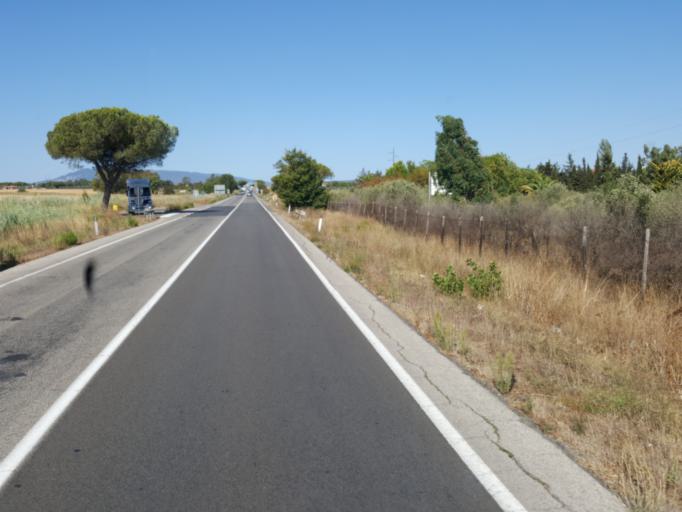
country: IT
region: Tuscany
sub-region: Provincia di Grosseto
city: Capalbio
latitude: 42.4150
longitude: 11.3836
